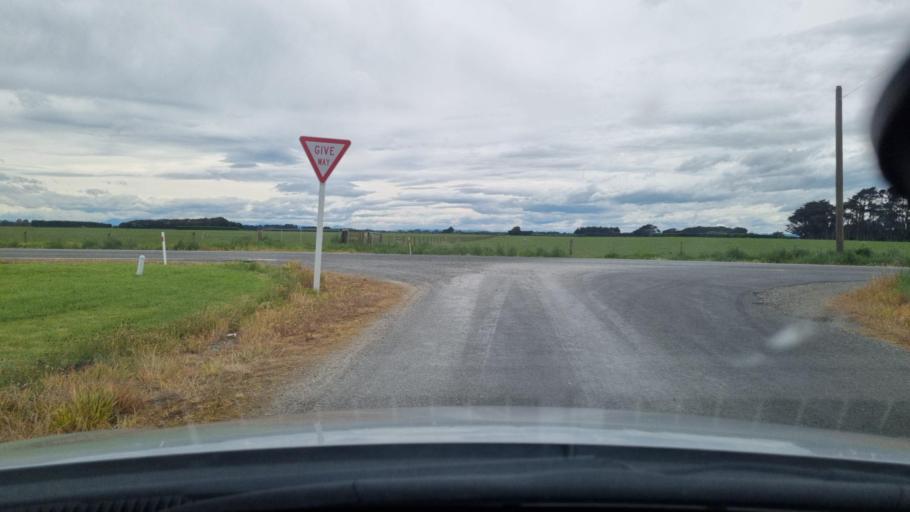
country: NZ
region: Southland
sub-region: Invercargill City
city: Invercargill
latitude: -46.3695
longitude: 168.2984
